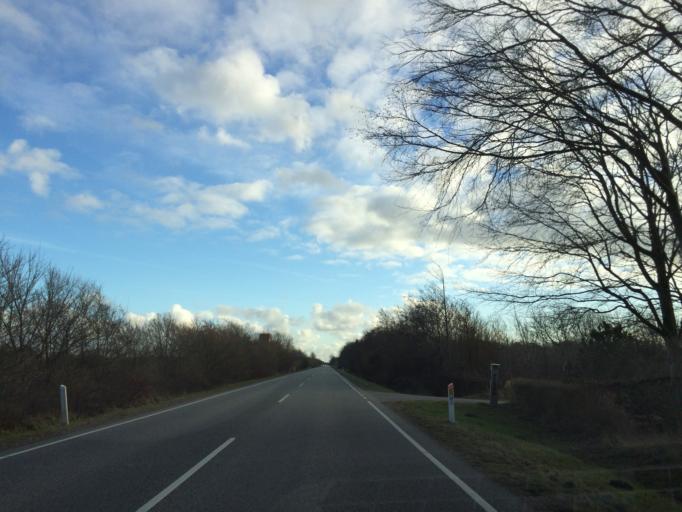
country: DK
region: Central Jutland
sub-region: Holstebro Kommune
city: Ulfborg
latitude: 56.3858
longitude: 8.3248
